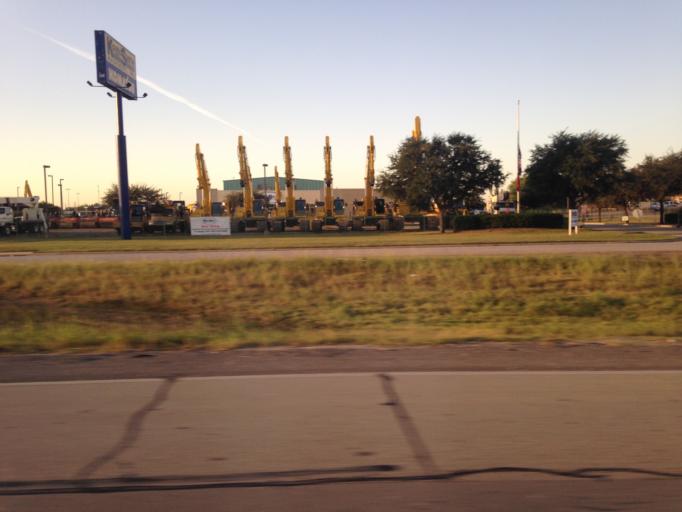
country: US
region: Texas
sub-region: Tarrant County
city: Blue Mound
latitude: 32.8415
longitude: -97.3364
